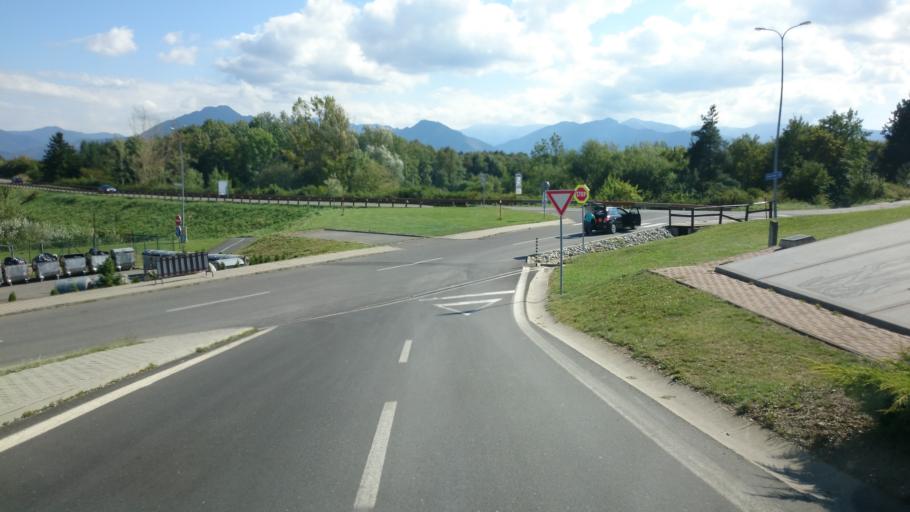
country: SK
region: Zilinsky
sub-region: Okres Liptovsky Mikulas
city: Liptovsky Mikulas
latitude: 49.1052
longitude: 19.5695
